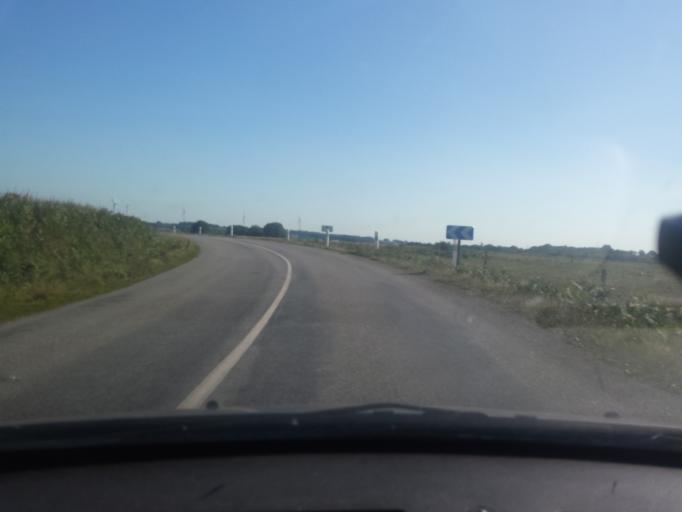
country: FR
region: Brittany
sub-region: Departement du Morbihan
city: Cleguerec
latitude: 48.1218
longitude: -3.1353
